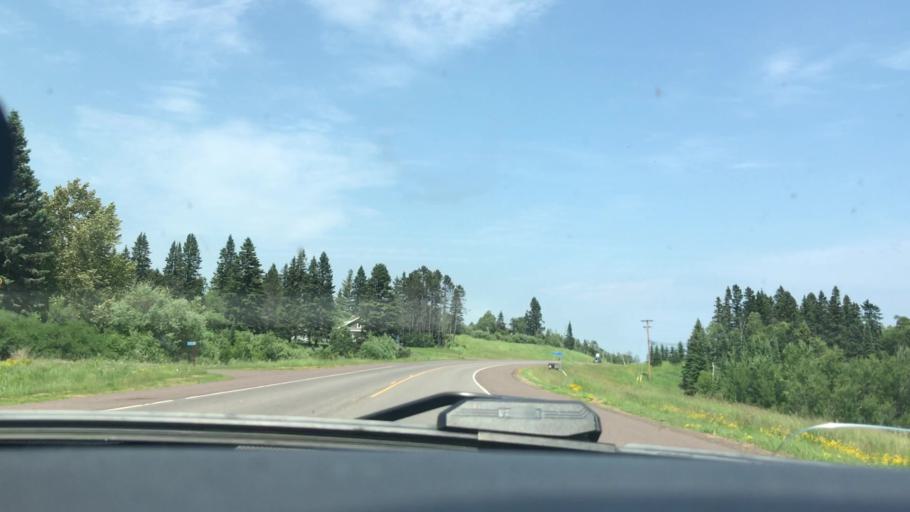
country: US
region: Minnesota
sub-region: Lake County
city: Silver Bay
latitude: 47.3179
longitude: -91.2230
